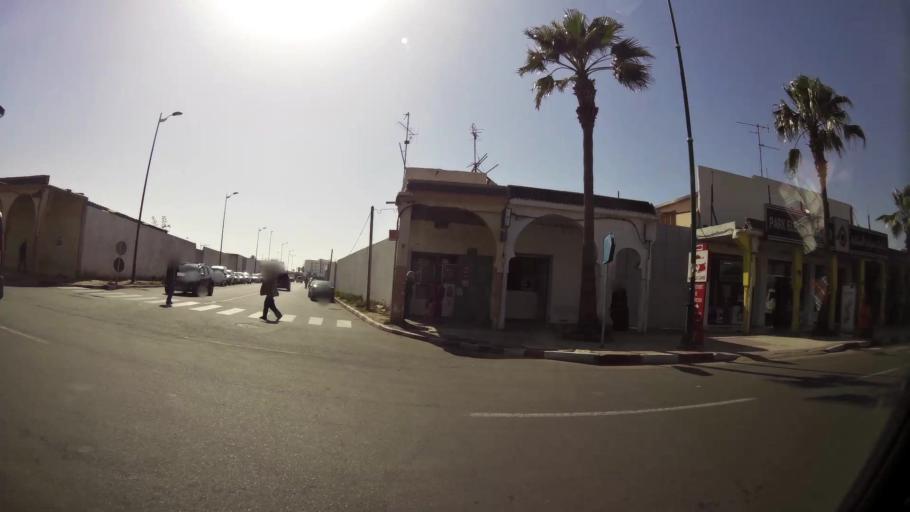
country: MA
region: Souss-Massa-Draa
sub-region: Inezgane-Ait Mellou
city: Inezgane
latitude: 30.3647
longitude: -9.5333
